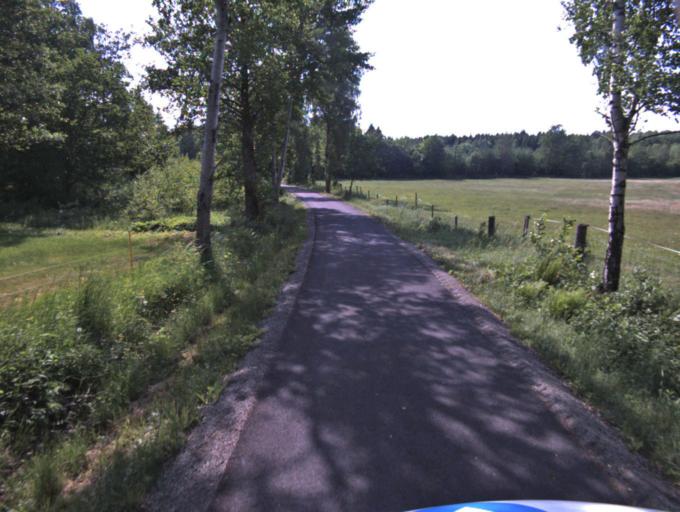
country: SE
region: Skane
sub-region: Kristianstads Kommun
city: Tollarp
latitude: 56.1993
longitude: 14.2838
